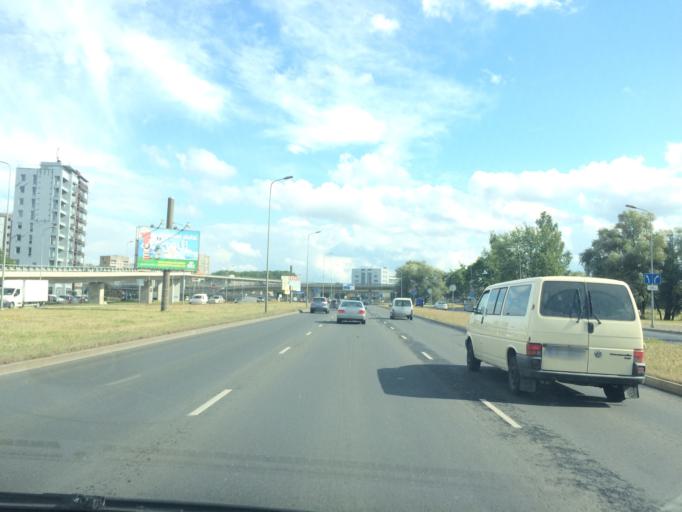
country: LV
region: Riga
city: Riga
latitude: 56.9243
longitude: 24.1632
